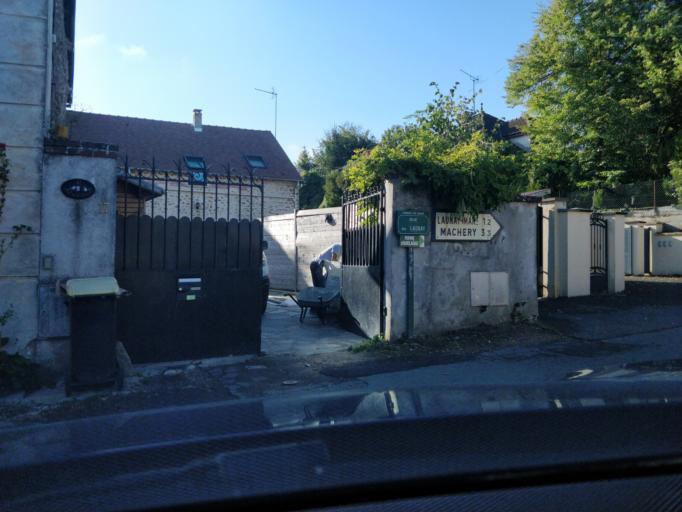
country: FR
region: Ile-de-France
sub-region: Departement de l'Essonne
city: Forges-les-Bains
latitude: 48.6246
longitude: 2.1023
